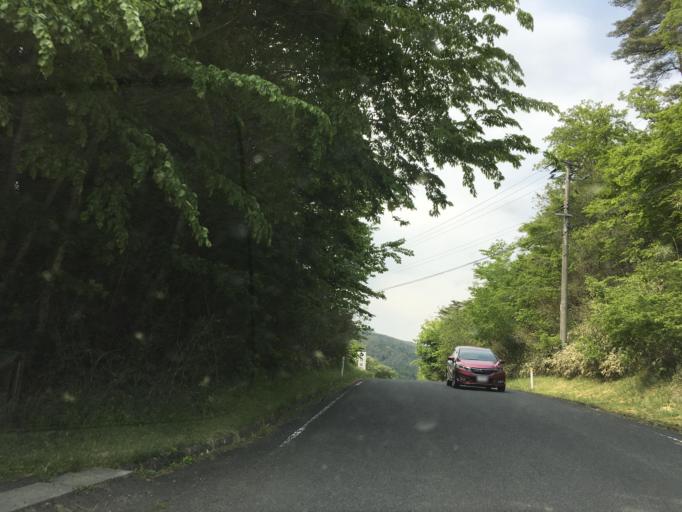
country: JP
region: Iwate
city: Ofunato
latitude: 38.8531
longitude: 141.5112
